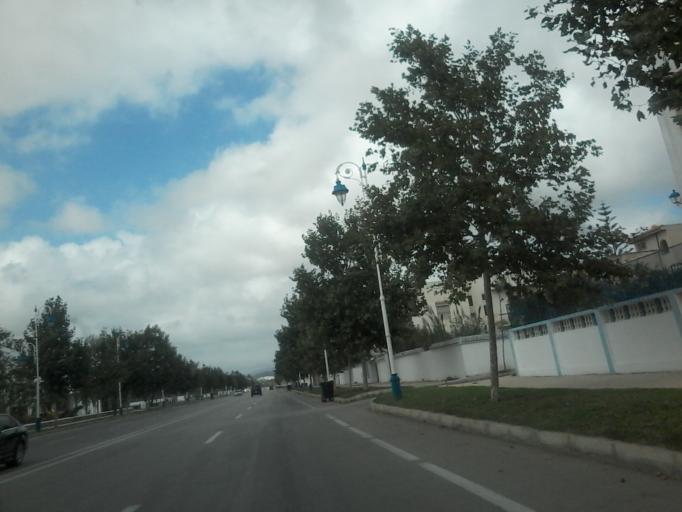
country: MA
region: Tanger-Tetouan
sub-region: Tetouan
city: Martil
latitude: 35.6343
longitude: -5.2873
